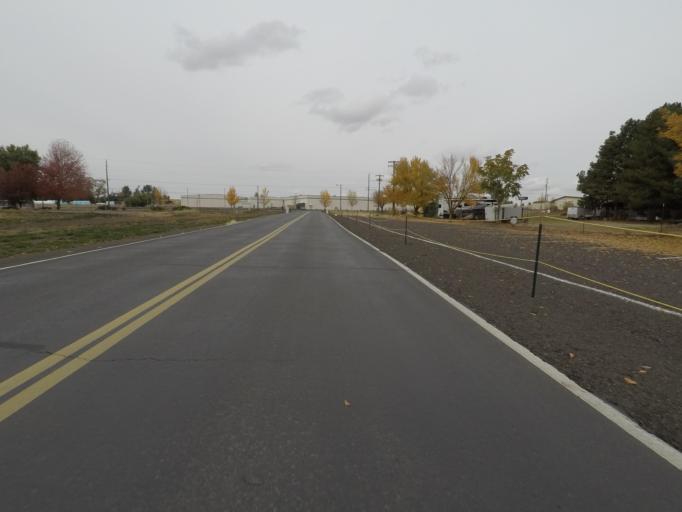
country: US
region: Washington
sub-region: Walla Walla County
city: Walla Walla East
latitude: 46.0811
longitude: -118.2749
